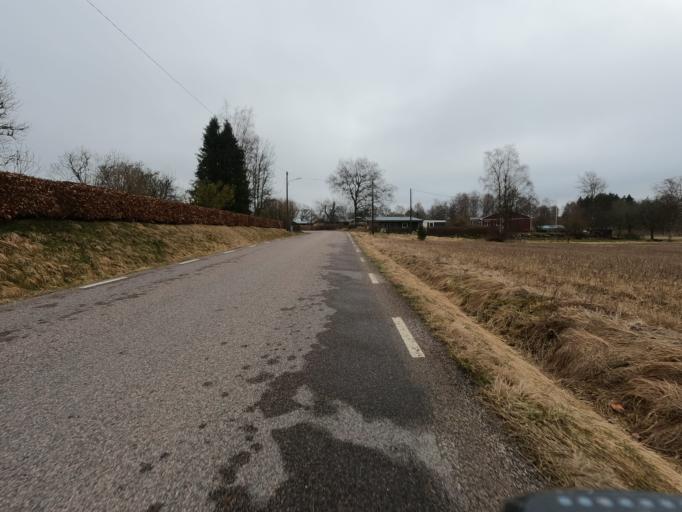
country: SE
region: Kronoberg
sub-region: Ljungby Kommun
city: Ljungby
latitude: 56.8288
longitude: 13.7566
